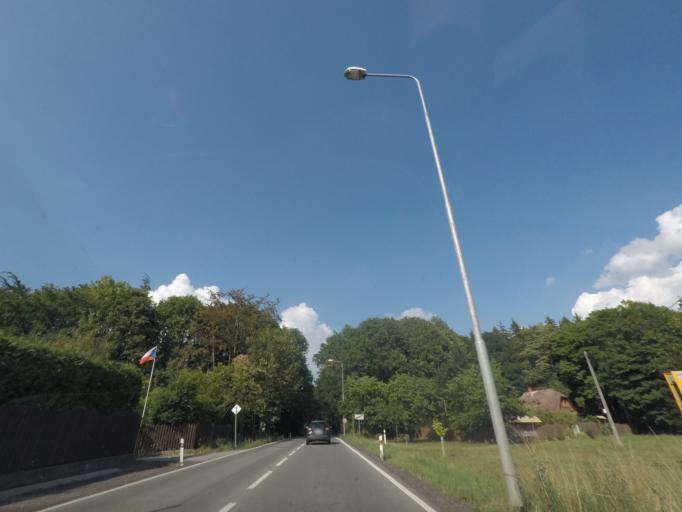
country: CZ
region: Kralovehradecky
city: Dvur Kralove nad Labem
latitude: 50.4628
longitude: 15.8631
